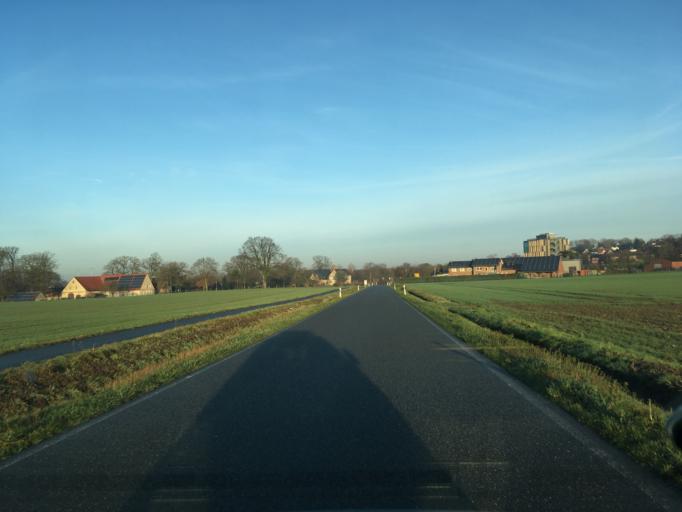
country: DE
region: North Rhine-Westphalia
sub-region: Regierungsbezirk Munster
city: Schoppingen
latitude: 52.0847
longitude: 7.2477
